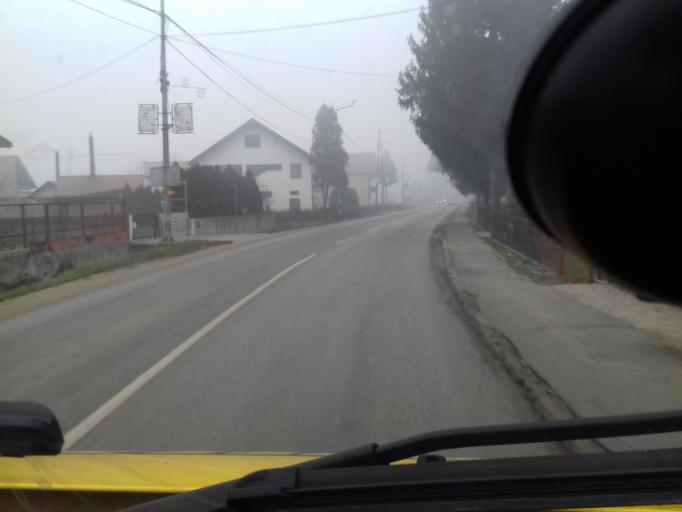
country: BA
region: Federation of Bosnia and Herzegovina
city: Vitez
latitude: 44.1469
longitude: 17.8023
